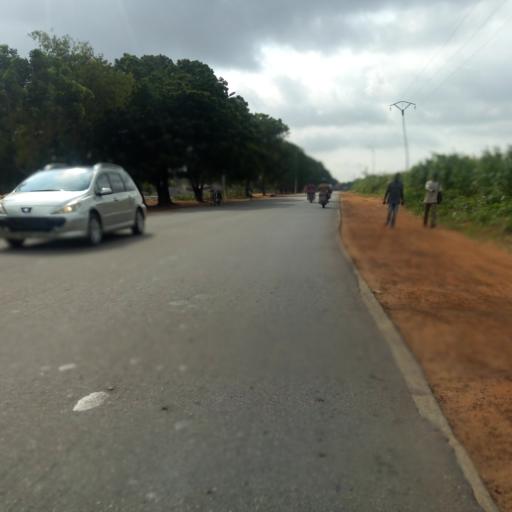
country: TG
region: Maritime
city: Lome
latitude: 6.1919
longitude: 1.2316
